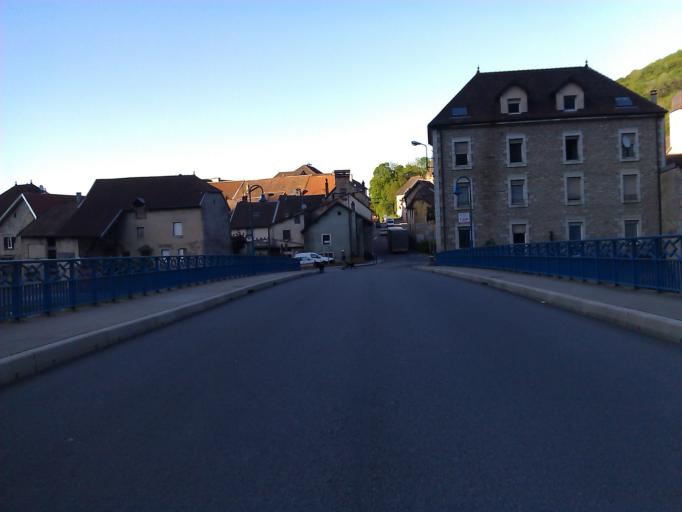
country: FR
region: Franche-Comte
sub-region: Departement du Doubs
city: Clerval
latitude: 47.3921
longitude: 6.4950
